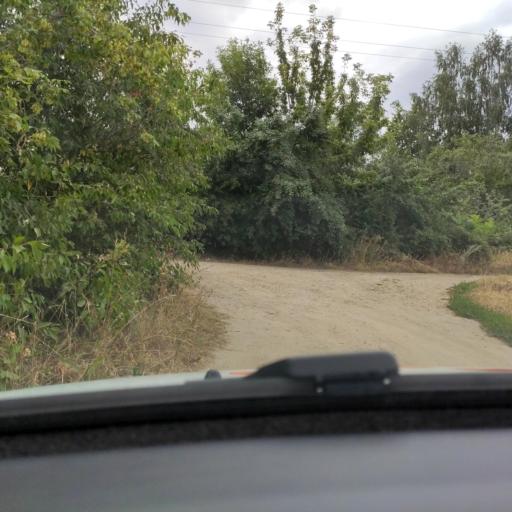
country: RU
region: Voronezj
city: Orlovo
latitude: 51.6491
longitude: 39.5672
